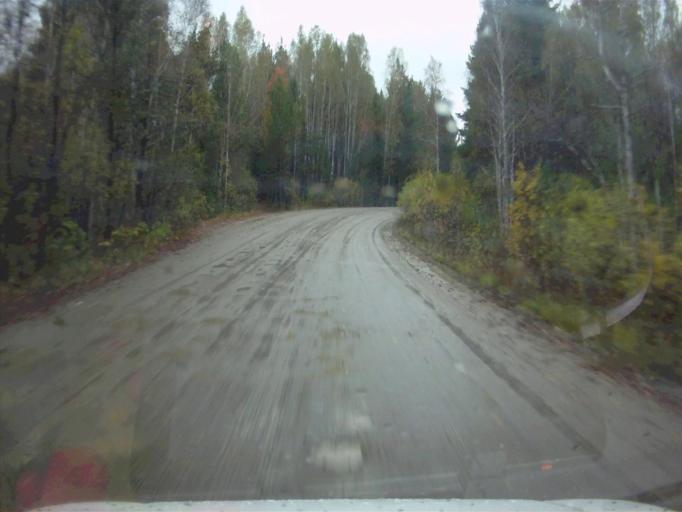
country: RU
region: Chelyabinsk
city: Kyshtym
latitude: 55.8342
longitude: 60.4857
